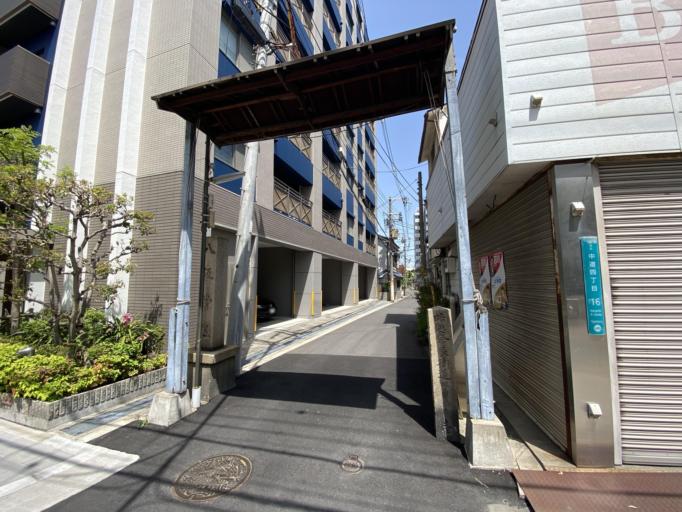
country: JP
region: Osaka
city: Osaka-shi
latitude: 34.6740
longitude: 135.5380
